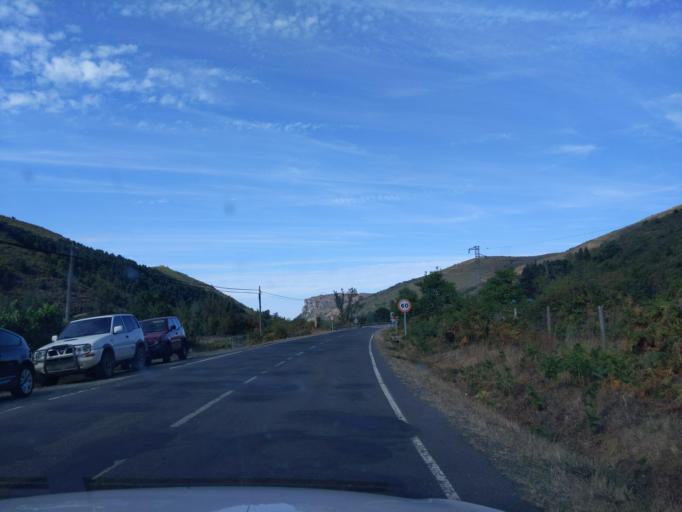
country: ES
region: La Rioja
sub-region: Provincia de La Rioja
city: Ezcaray
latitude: 42.3035
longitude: -3.0231
